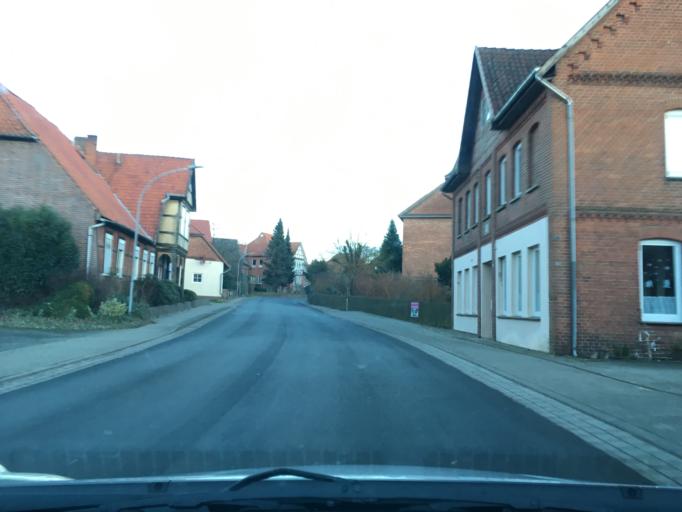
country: DE
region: Lower Saxony
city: Ratzlingen
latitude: 52.9760
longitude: 10.6716
